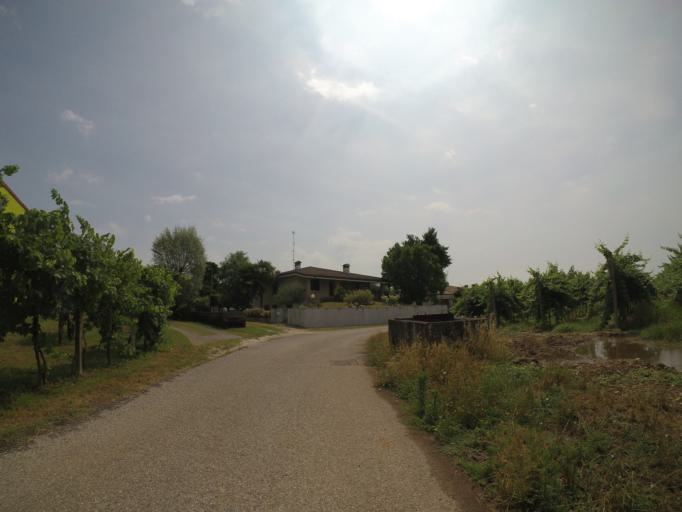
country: IT
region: Friuli Venezia Giulia
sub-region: Provincia di Udine
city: Bertiolo
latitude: 45.9422
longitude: 13.0575
